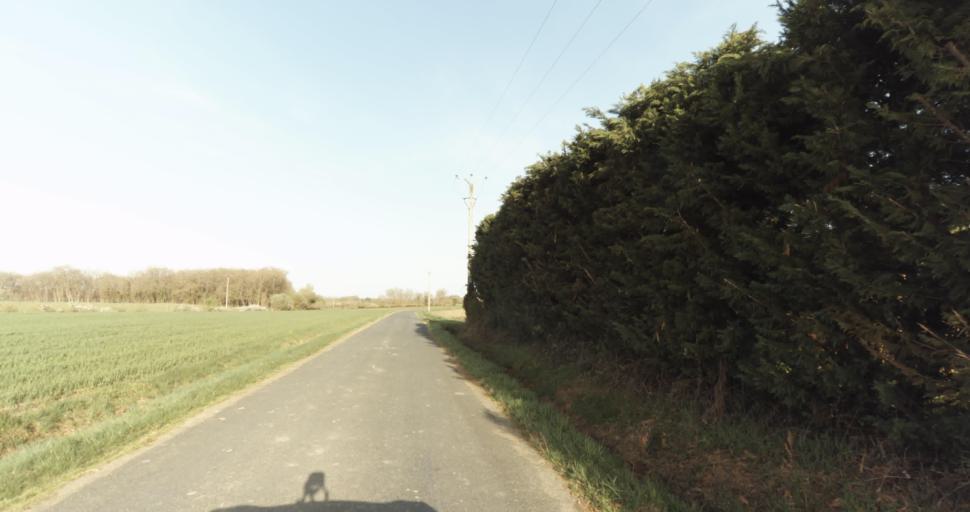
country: FR
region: Midi-Pyrenees
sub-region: Departement du Tarn
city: Saint-Sulpice-la-Pointe
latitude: 43.7314
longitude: 1.6980
